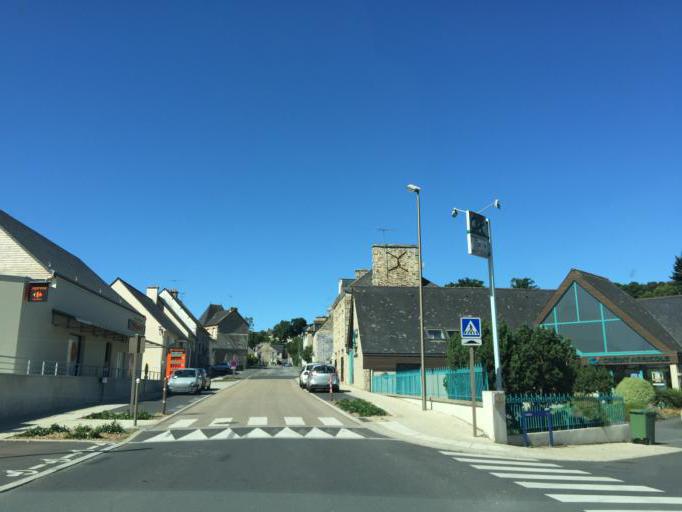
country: FR
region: Brittany
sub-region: Departement des Cotes-d'Armor
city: Jugon-les-Lacs
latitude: 48.4092
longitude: -2.3232
